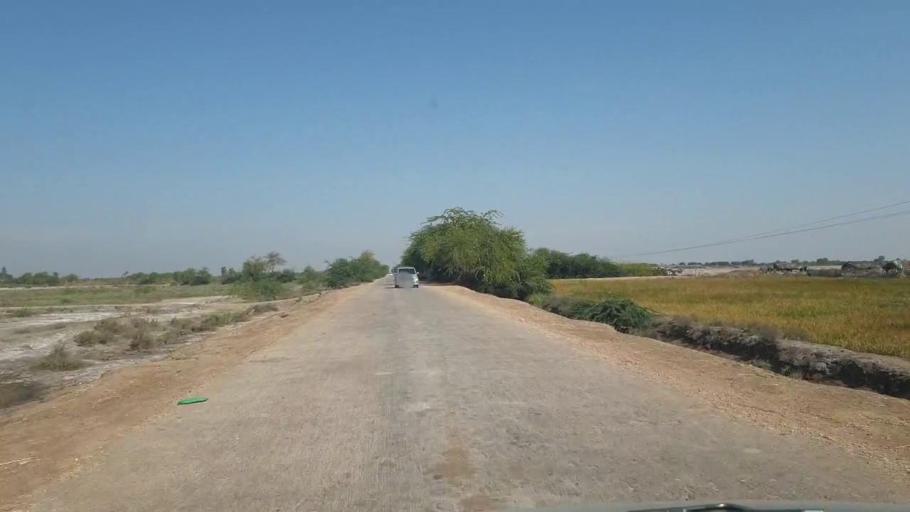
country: PK
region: Sindh
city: Tando Bago
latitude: 24.8104
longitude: 68.9813
